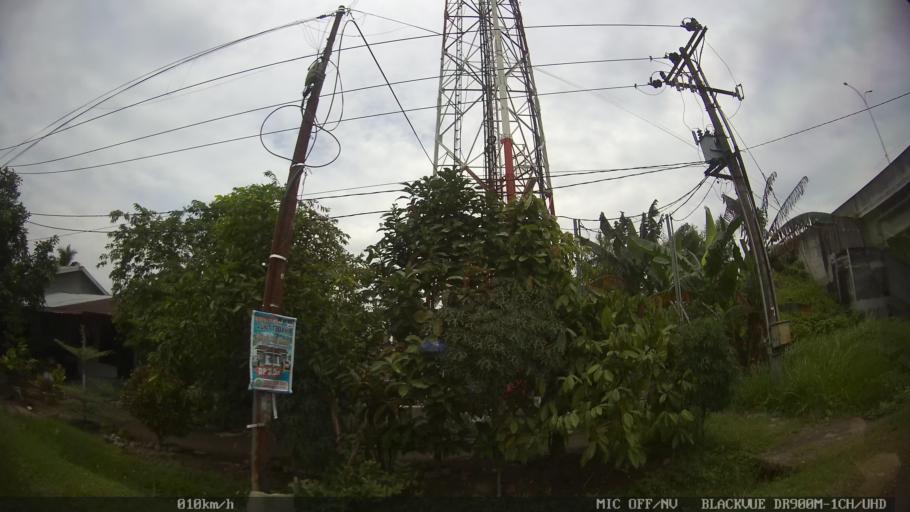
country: ID
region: North Sumatra
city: Binjai
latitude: 3.6469
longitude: 98.5509
